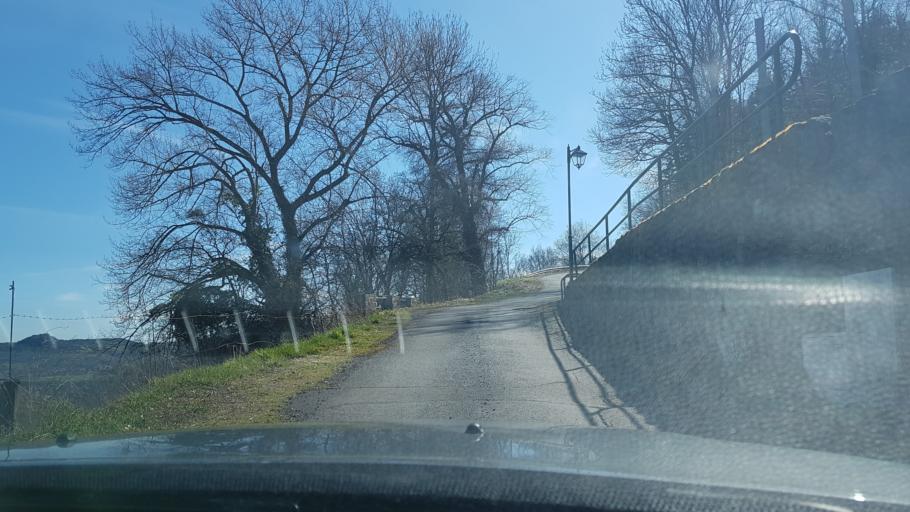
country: FR
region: Auvergne
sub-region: Departement du Puy-de-Dome
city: Aydat
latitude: 45.5391
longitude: 2.9925
